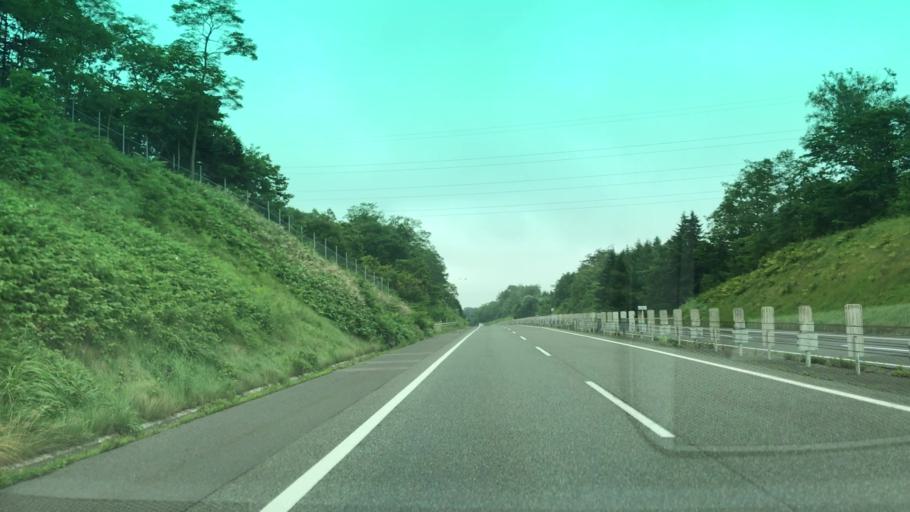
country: JP
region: Hokkaido
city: Tomakomai
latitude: 42.6519
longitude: 141.5544
